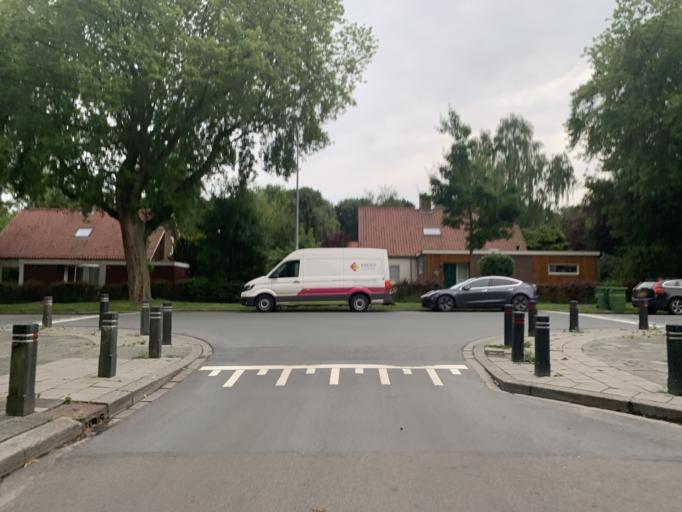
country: NL
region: Groningen
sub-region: Gemeente Groningen
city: Oosterpark
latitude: 53.1970
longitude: 6.5890
